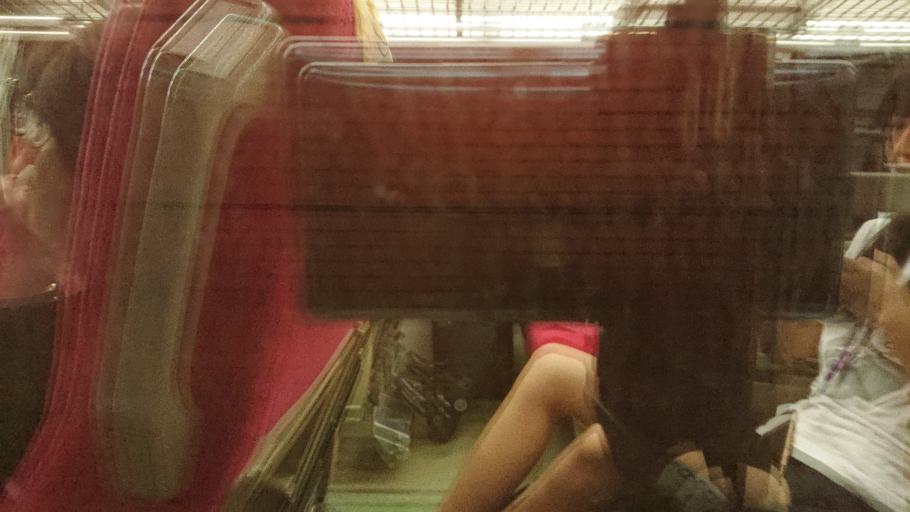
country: TW
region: Taiwan
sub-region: Keelung
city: Keelung
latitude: 24.9559
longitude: 121.9166
